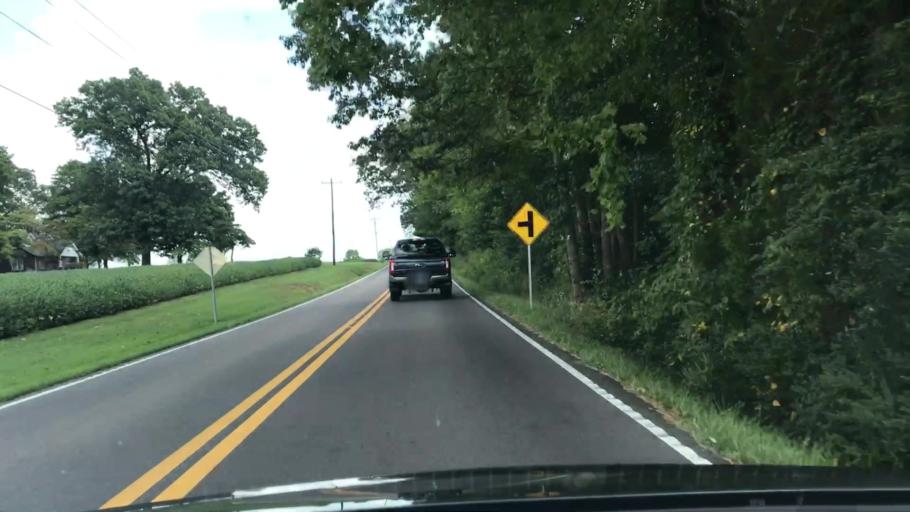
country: US
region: Tennessee
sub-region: Robertson County
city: Springfield
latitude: 36.5551
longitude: -86.8235
